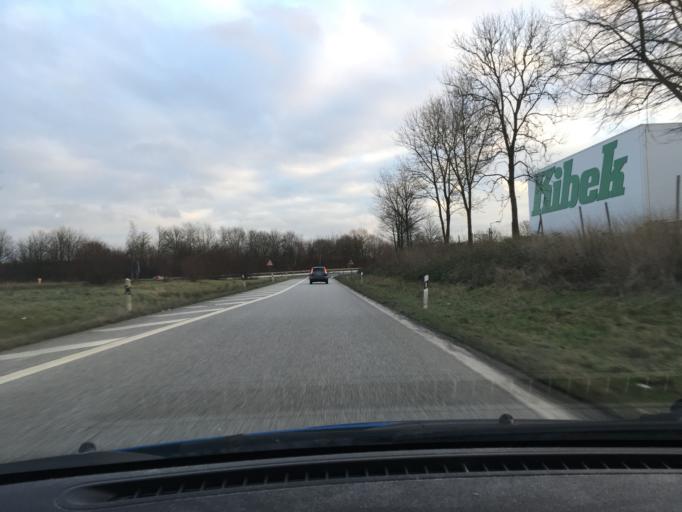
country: DE
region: Schleswig-Holstein
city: Seeth-Ekholt
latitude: 53.7431
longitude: 9.7114
